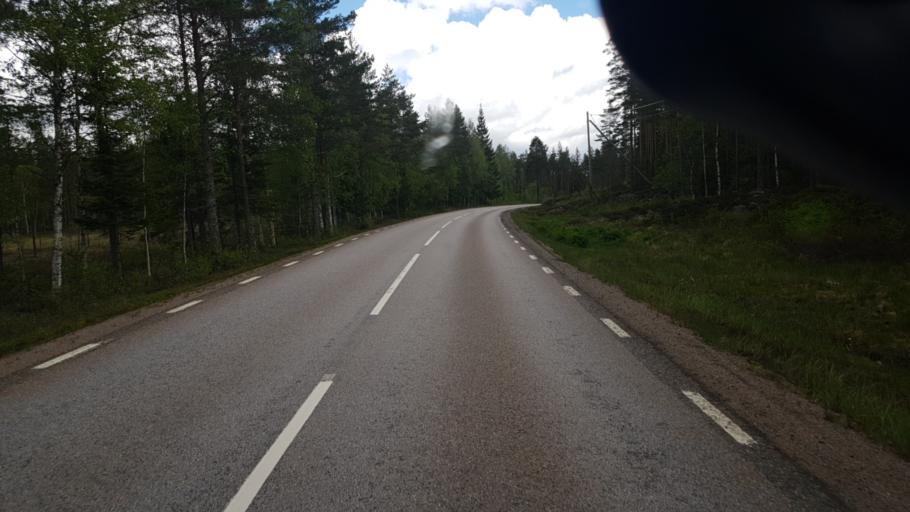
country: SE
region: Vaermland
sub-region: Arjangs Kommun
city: Arjaeng
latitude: 59.5627
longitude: 12.1832
